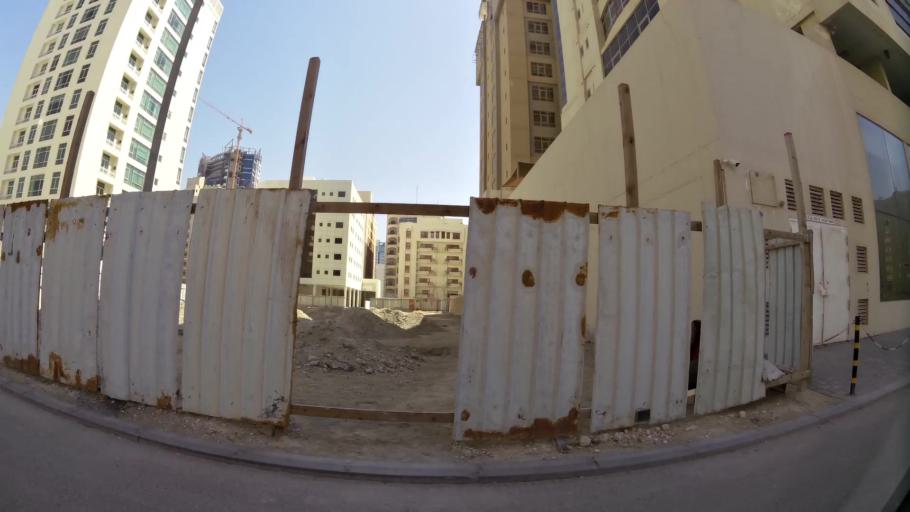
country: BH
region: Manama
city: Manama
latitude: 26.2143
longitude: 50.6063
